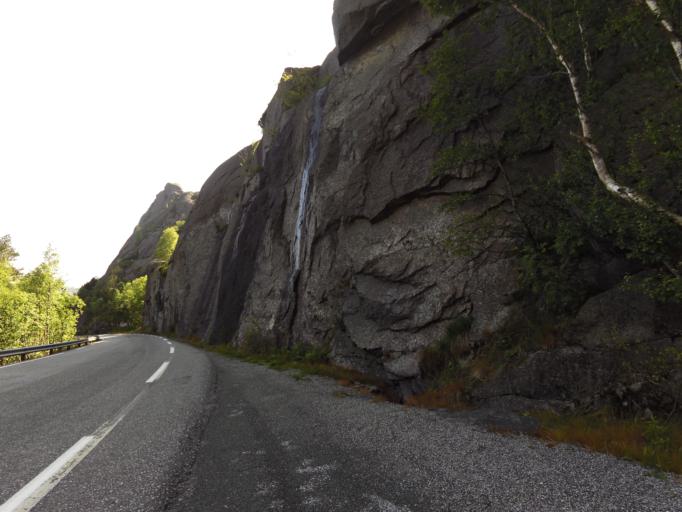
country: NO
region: Rogaland
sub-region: Sokndal
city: Hauge i Dalane
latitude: 58.3316
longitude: 6.3505
